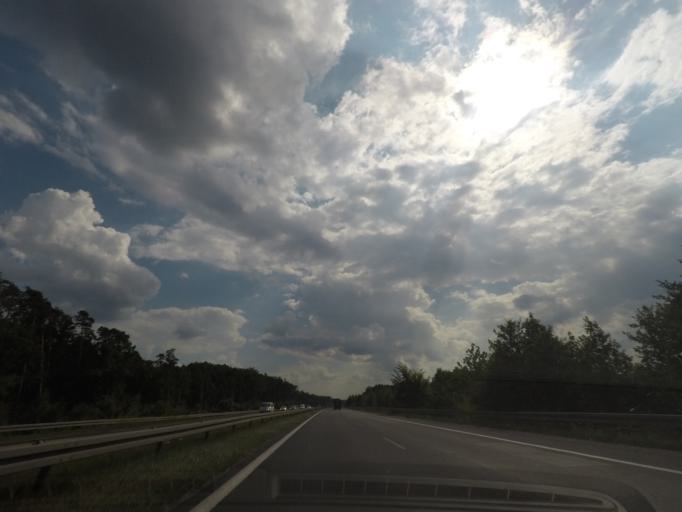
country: PL
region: Lodz Voivodeship
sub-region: Powiat radomszczanski
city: Gomunice
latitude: 51.1731
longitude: 19.4643
